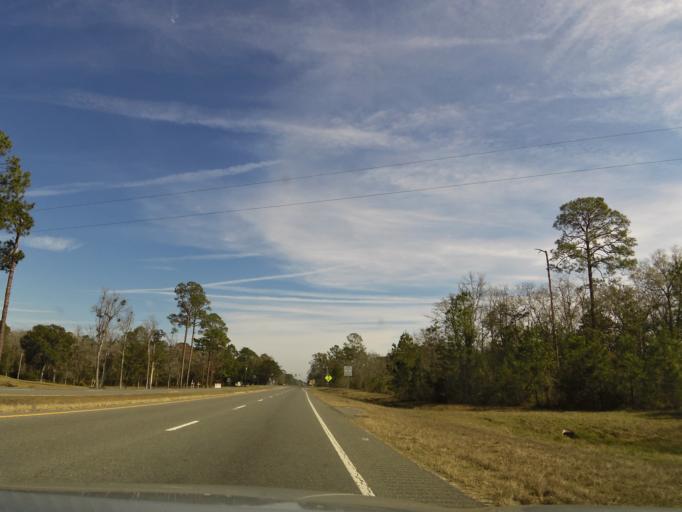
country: US
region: Georgia
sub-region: Brantley County
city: Nahunta
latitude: 31.2286
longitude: -81.7957
